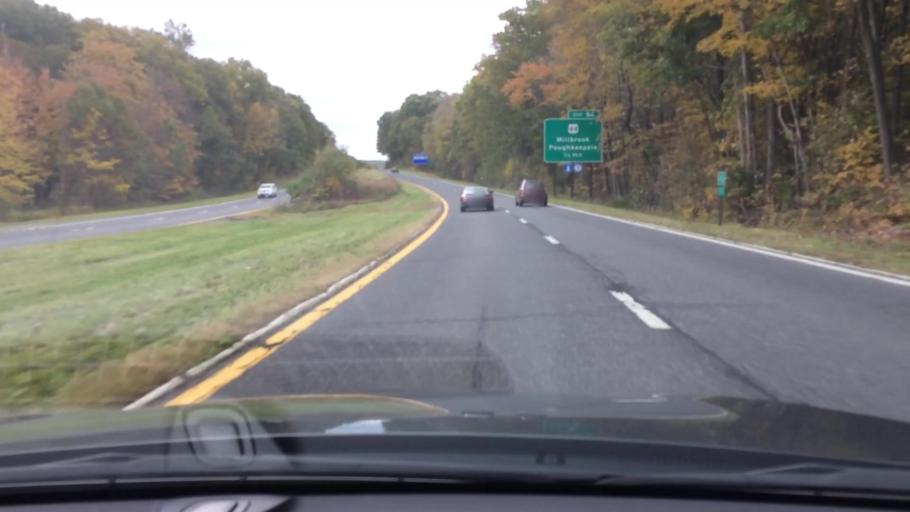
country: US
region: New York
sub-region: Dutchess County
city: Pleasant Valley
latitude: 41.7862
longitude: -73.7699
